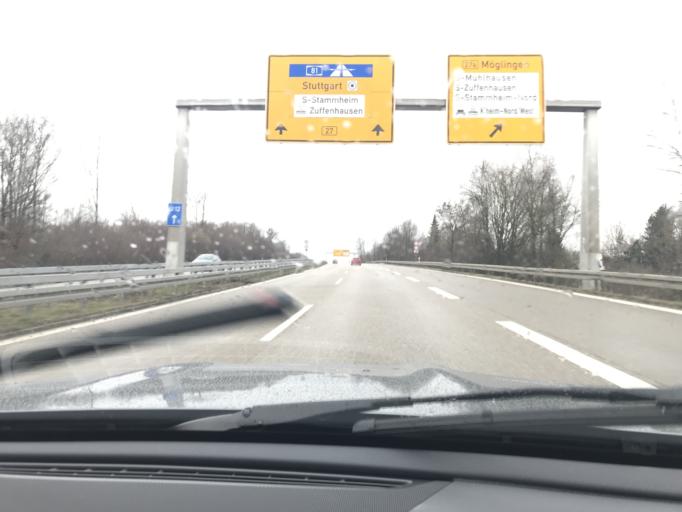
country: DE
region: Baden-Wuerttemberg
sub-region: Regierungsbezirk Stuttgart
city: Kornwestheim
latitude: 48.8473
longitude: 9.1813
